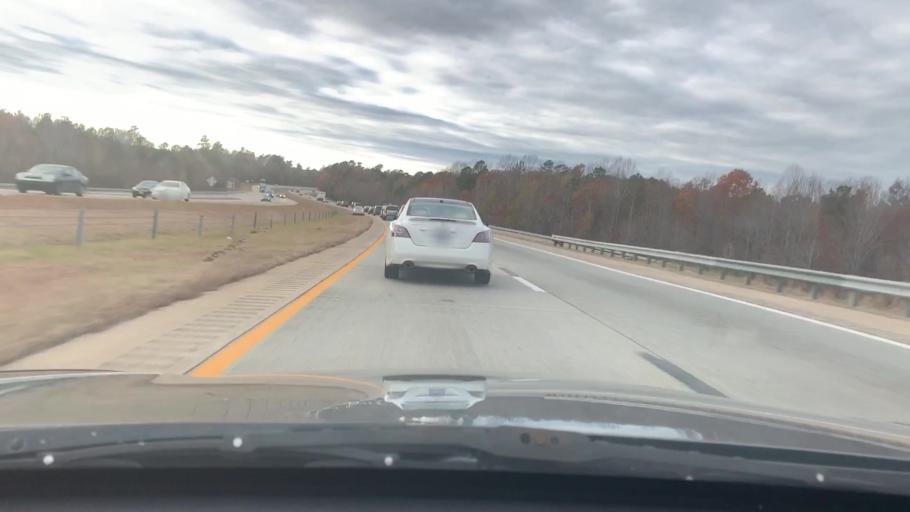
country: US
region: North Carolina
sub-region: Orange County
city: Hillsborough
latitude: 36.0374
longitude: -79.0988
